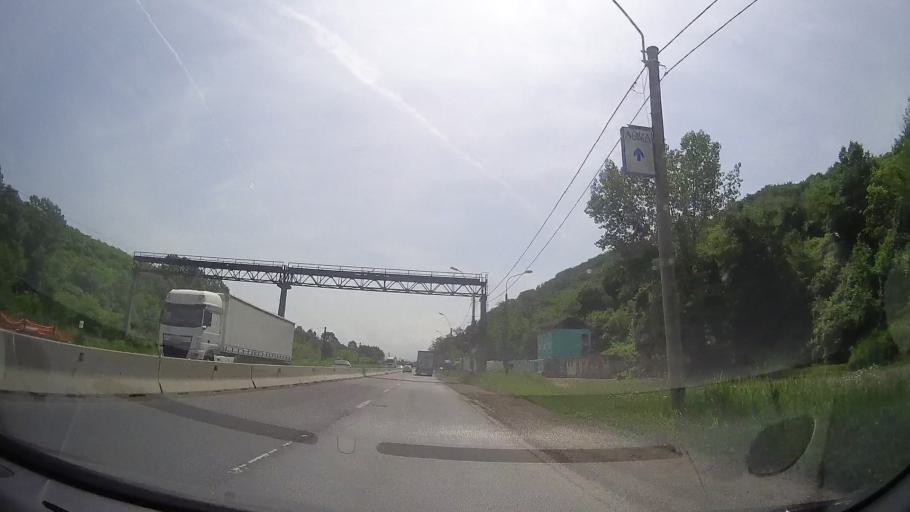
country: RO
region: Hunedoara
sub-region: Comuna Soimus
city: Soimus
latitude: 45.9046
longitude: 22.8801
